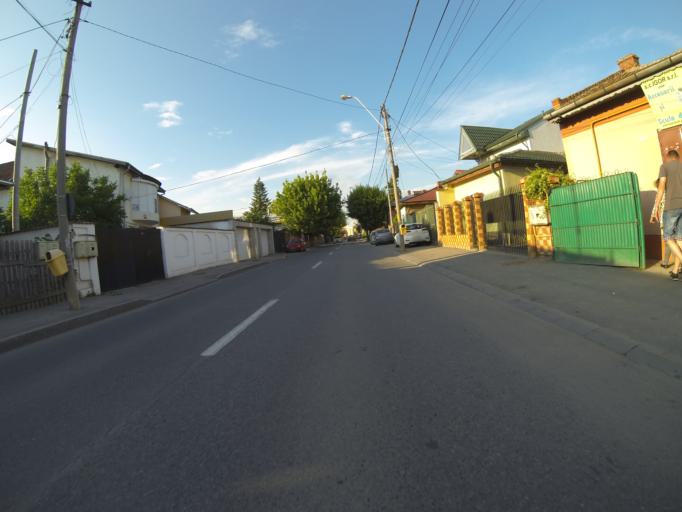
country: RO
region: Dolj
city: Craiova
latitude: 44.3043
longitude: 23.8017
